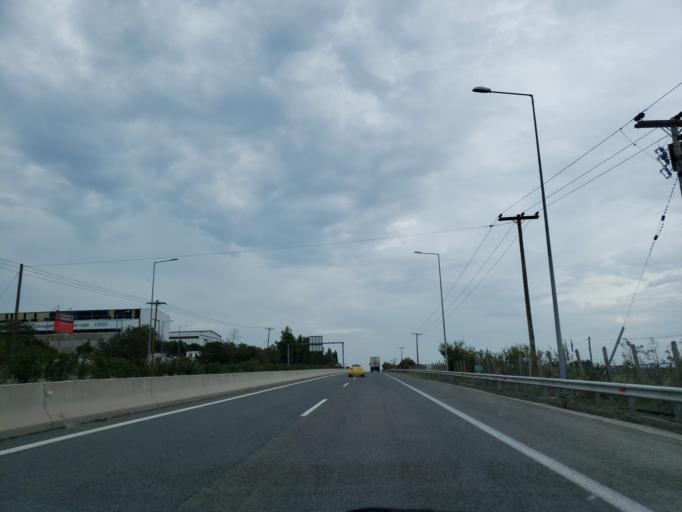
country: GR
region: Central Greece
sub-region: Nomos Voiotias
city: Arma
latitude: 38.3742
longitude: 23.5122
